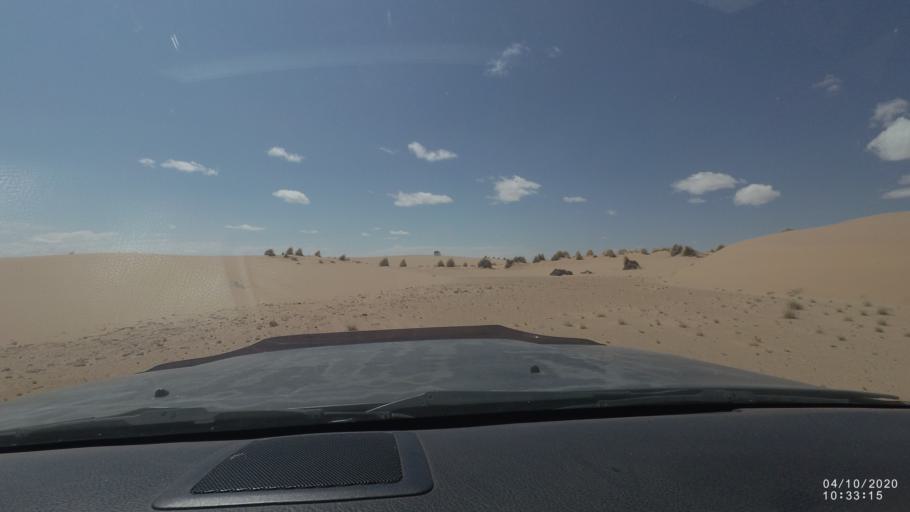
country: BO
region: Oruro
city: Poopo
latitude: -18.7045
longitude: -67.4804
